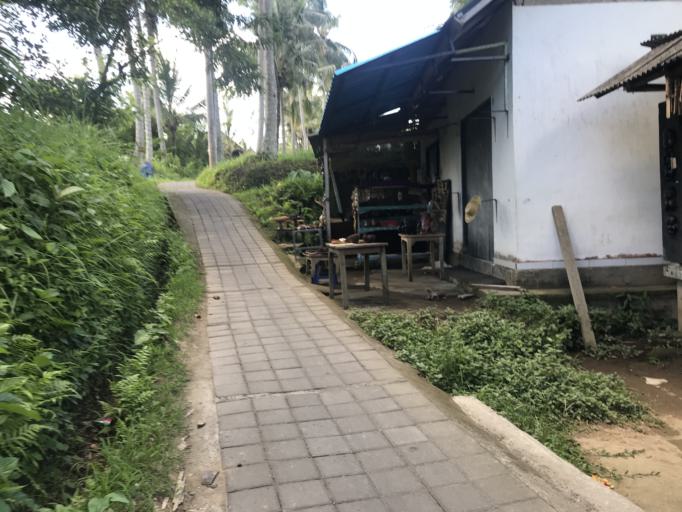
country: ID
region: Bali
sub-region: Kabupaten Gianyar
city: Ubud
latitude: -8.5006
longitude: 115.2585
